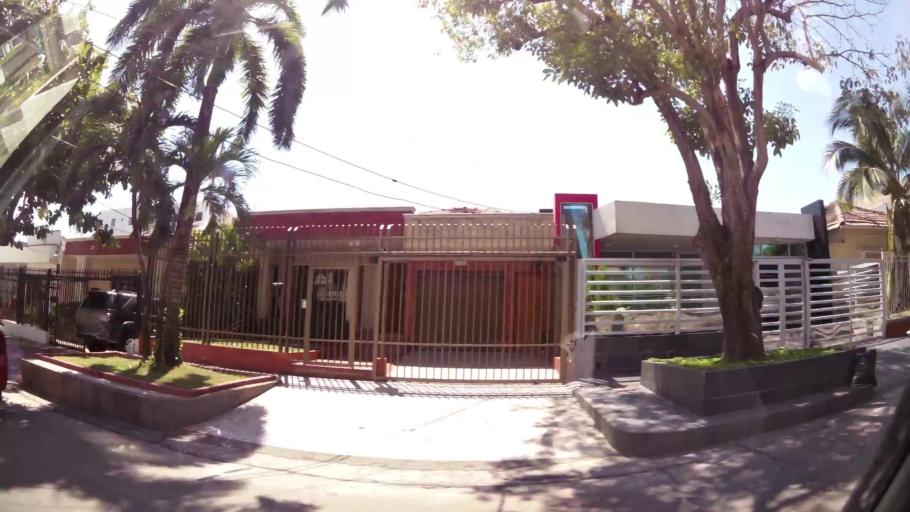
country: CO
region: Atlantico
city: Barranquilla
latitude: 10.9978
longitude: -74.8135
